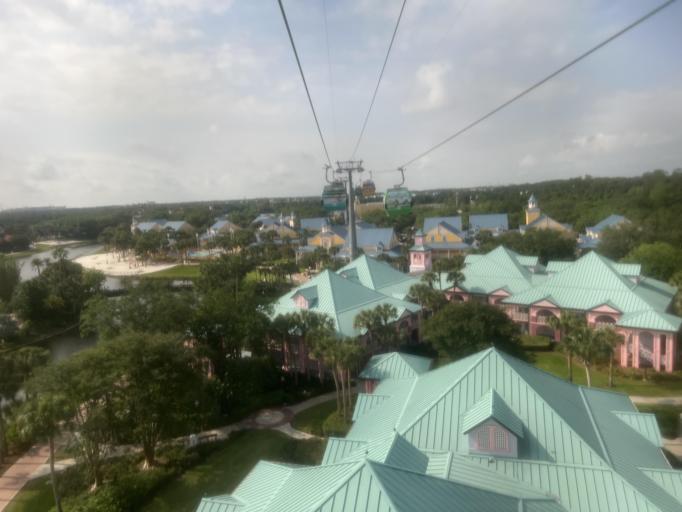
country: US
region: Florida
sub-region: Osceola County
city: Celebration
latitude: 28.3634
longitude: -81.5443
